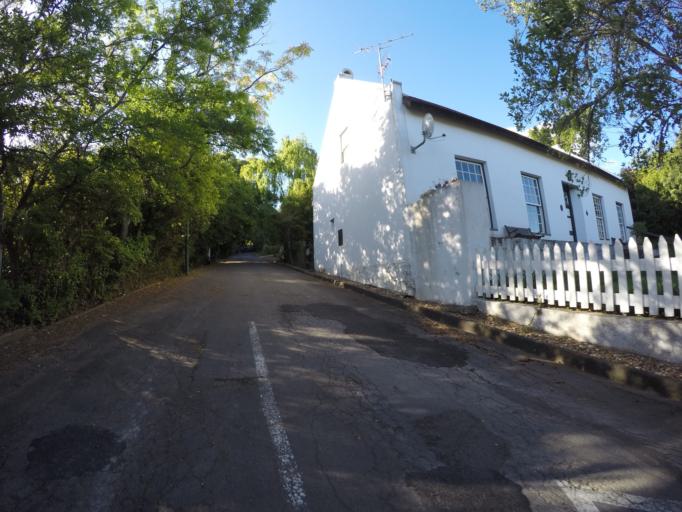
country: ZA
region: Western Cape
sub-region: Overberg District Municipality
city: Swellendam
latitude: -34.0165
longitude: 20.4486
